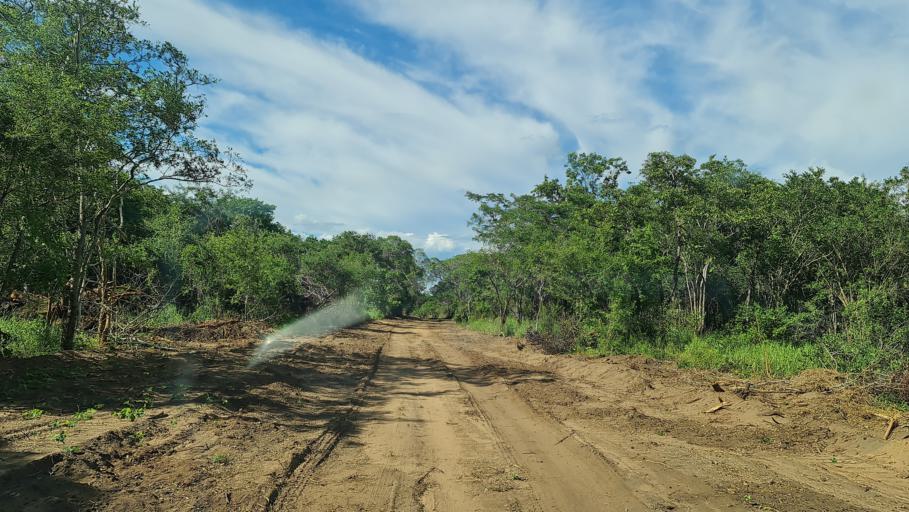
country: MZ
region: Nampula
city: Antonio Enes
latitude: -15.5226
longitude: 40.1278
